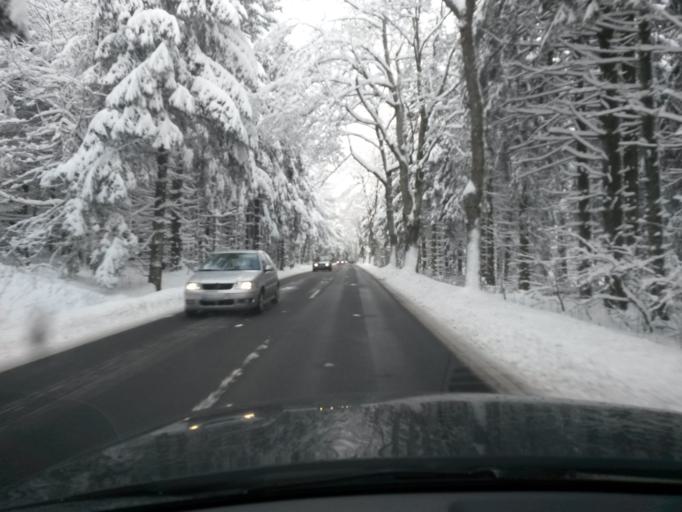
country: DE
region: Bavaria
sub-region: Regierungsbezirk Unterfranken
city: Bischofsheim an der Rhon
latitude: 50.4458
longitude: 9.9803
